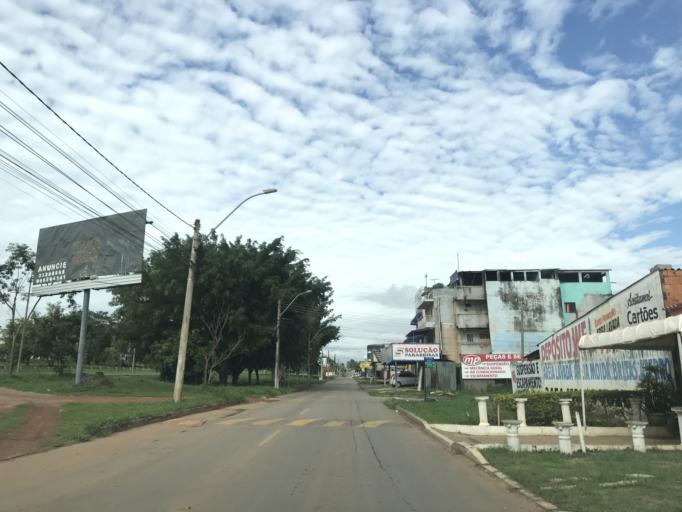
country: BR
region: Federal District
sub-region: Brasilia
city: Brasilia
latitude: -15.6618
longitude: -47.7983
